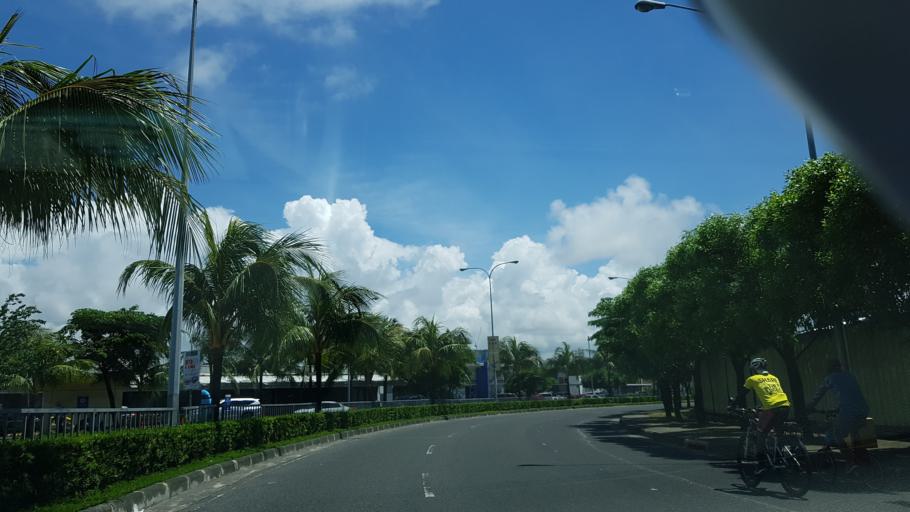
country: PH
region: Metro Manila
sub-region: City of Manila
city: Port Area
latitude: 14.5407
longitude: 120.9796
